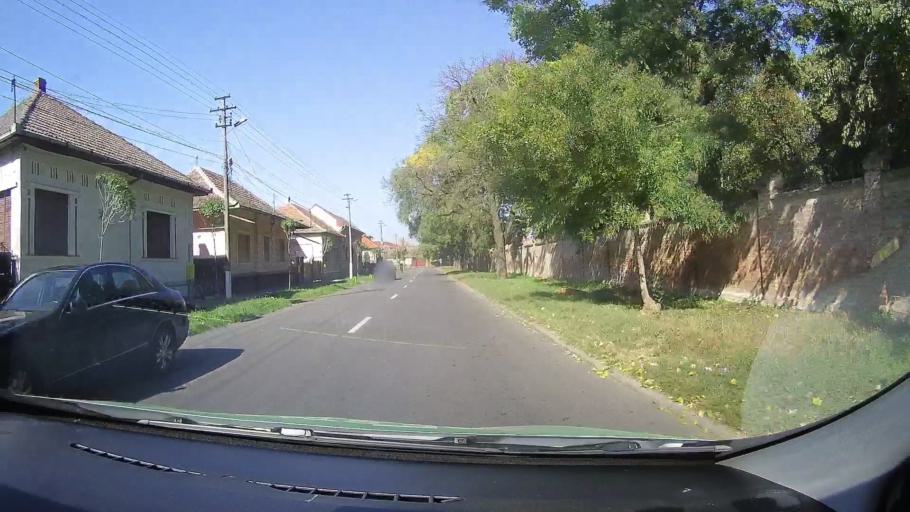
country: RO
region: Satu Mare
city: Carei
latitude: 47.6821
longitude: 22.4639
